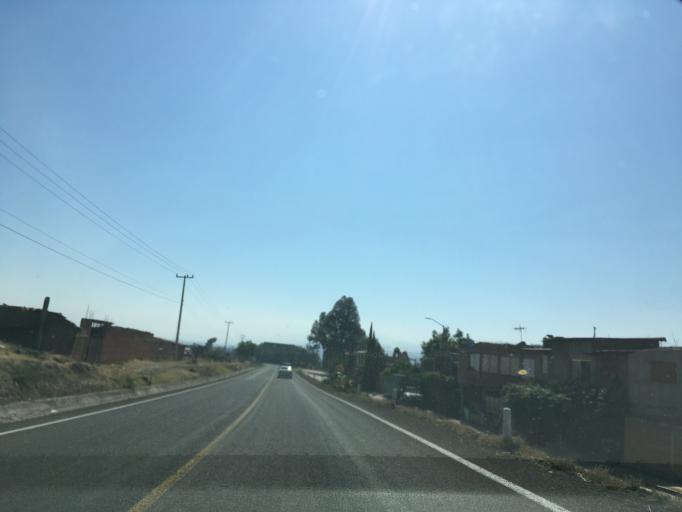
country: MX
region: Michoacan
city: Indaparapeo
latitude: 19.7912
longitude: -100.9623
